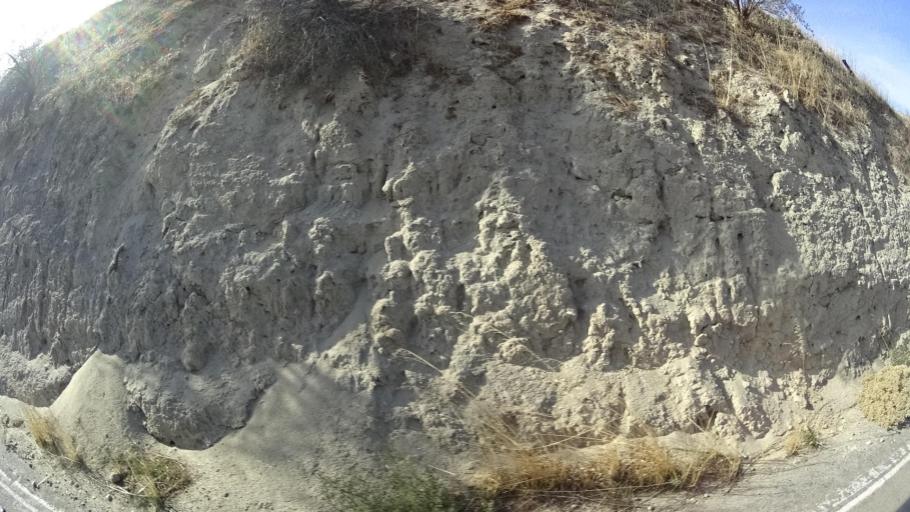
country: US
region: California
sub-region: Kern County
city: Oildale
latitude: 35.5436
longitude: -118.9591
